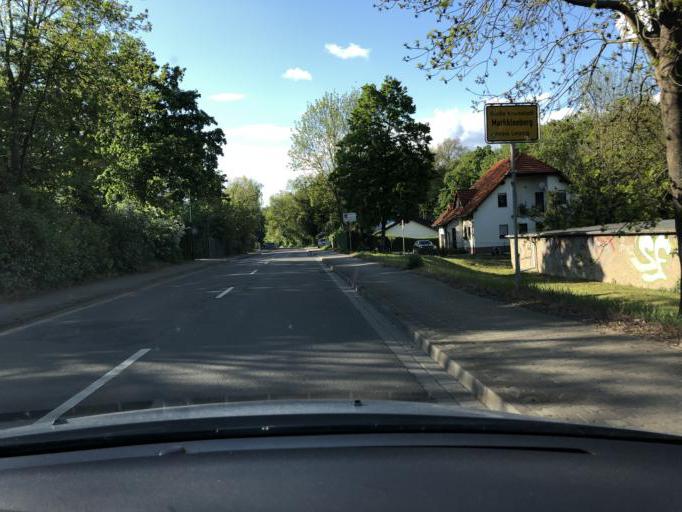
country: DE
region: Saxony
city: Markkleeberg
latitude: 51.2441
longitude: 12.3844
